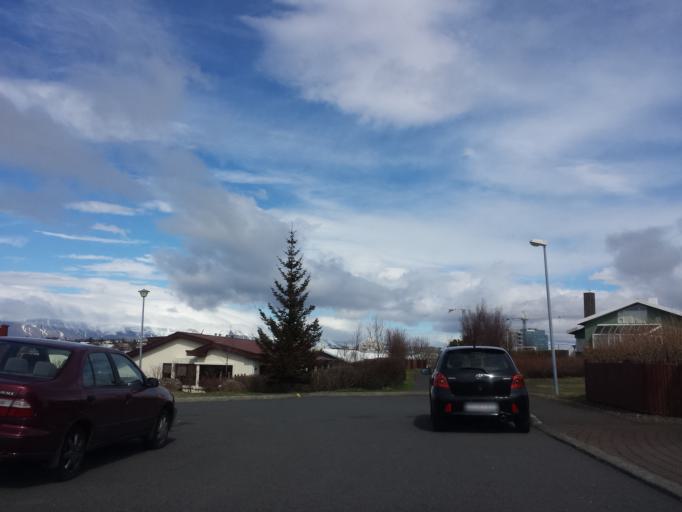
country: IS
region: Capital Region
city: Kopavogur
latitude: 64.0992
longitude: -21.8971
